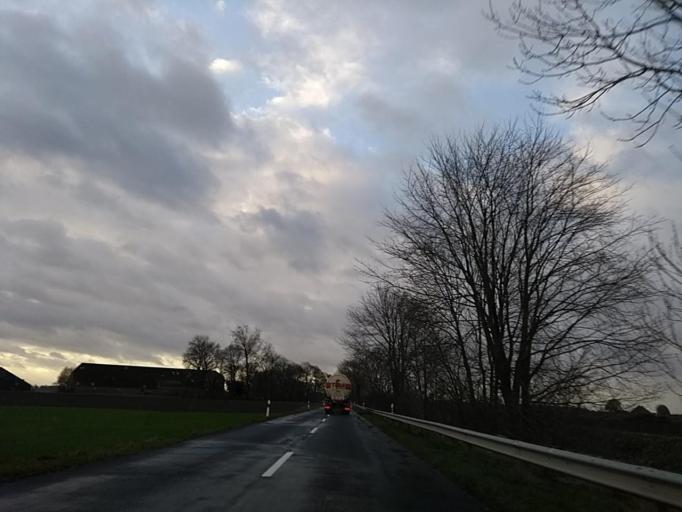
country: DE
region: Lower Saxony
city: Bunde
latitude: 53.2038
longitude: 7.2198
